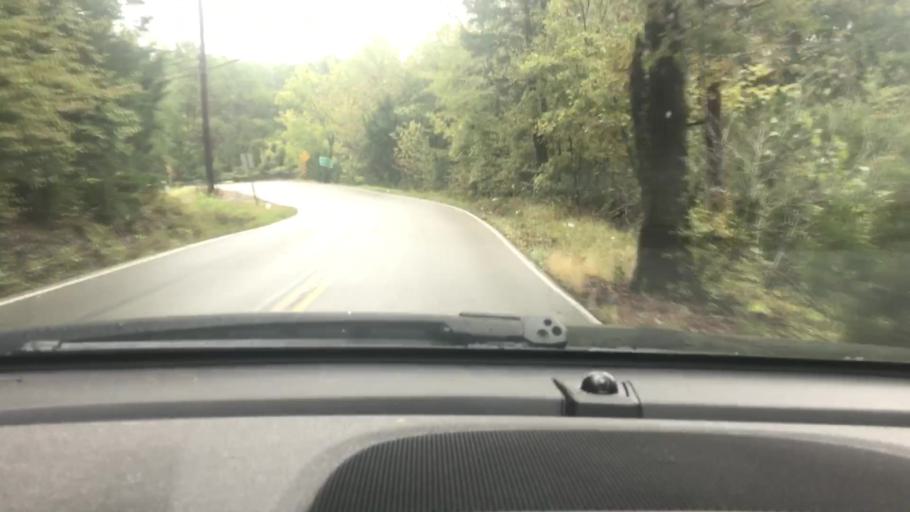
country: US
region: Tennessee
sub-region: Cheatham County
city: Kingston Springs
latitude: 36.1001
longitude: -87.1337
